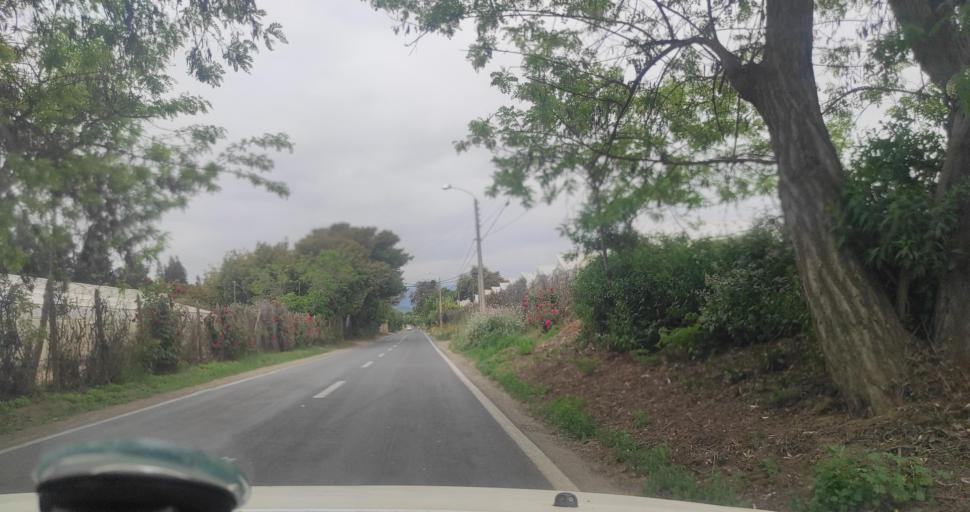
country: CL
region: Valparaiso
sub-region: Provincia de Marga Marga
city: Limache
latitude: -33.0163
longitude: -71.2376
